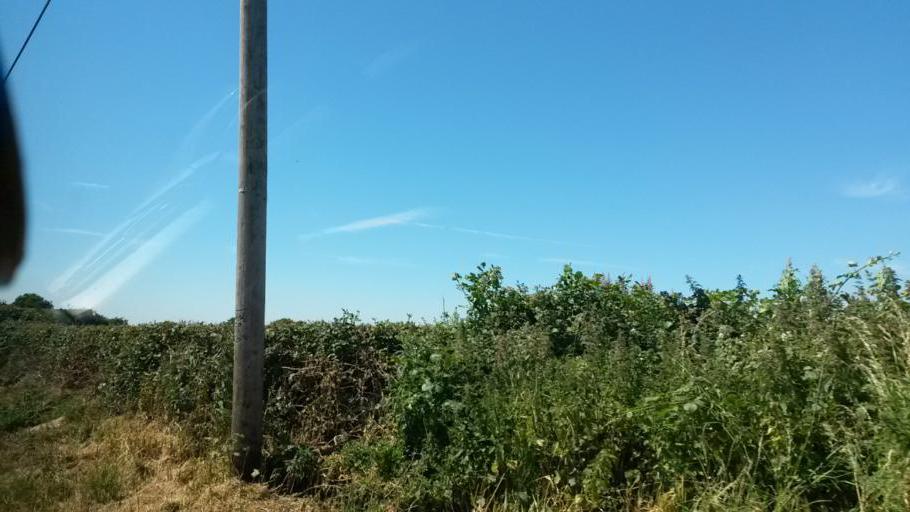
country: IE
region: Leinster
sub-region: Dublin City
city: Finglas
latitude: 53.4364
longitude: -6.3113
